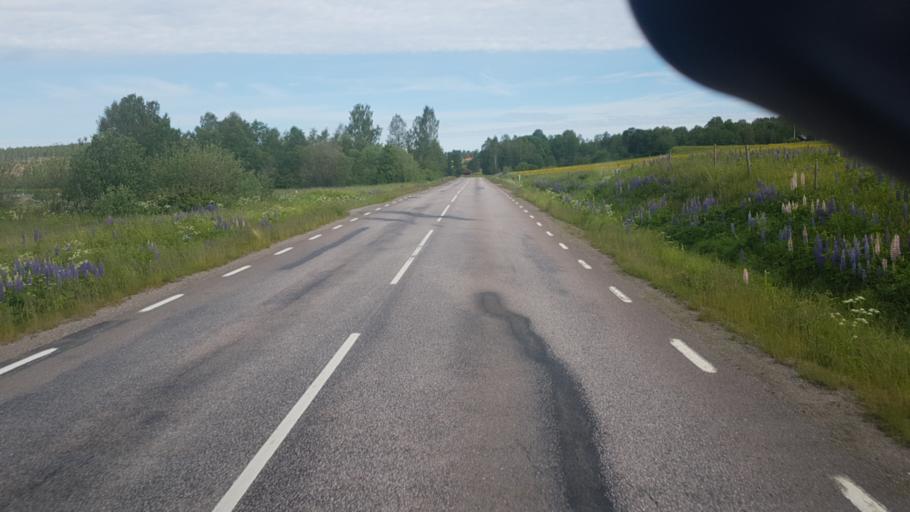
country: SE
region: Vaermland
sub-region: Arvika Kommun
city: Arvika
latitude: 59.7893
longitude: 12.6206
